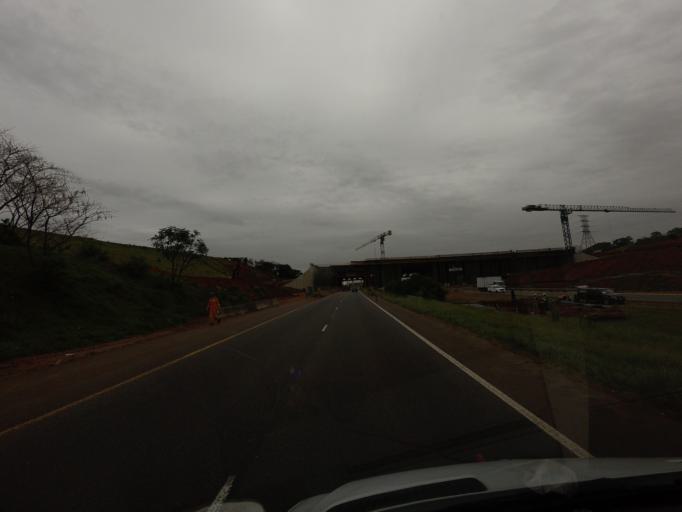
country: ZA
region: KwaZulu-Natal
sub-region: eThekwini Metropolitan Municipality
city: Durban
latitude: -29.7139
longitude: 31.0645
